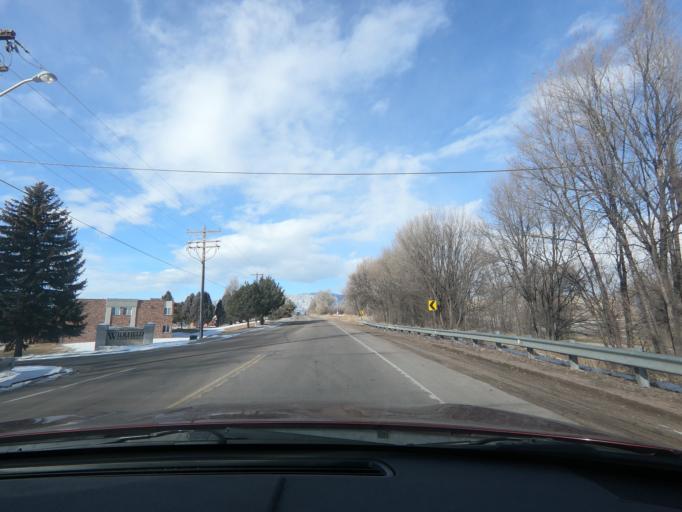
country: US
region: Colorado
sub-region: El Paso County
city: Security-Widefield
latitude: 38.7373
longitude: -104.7119
